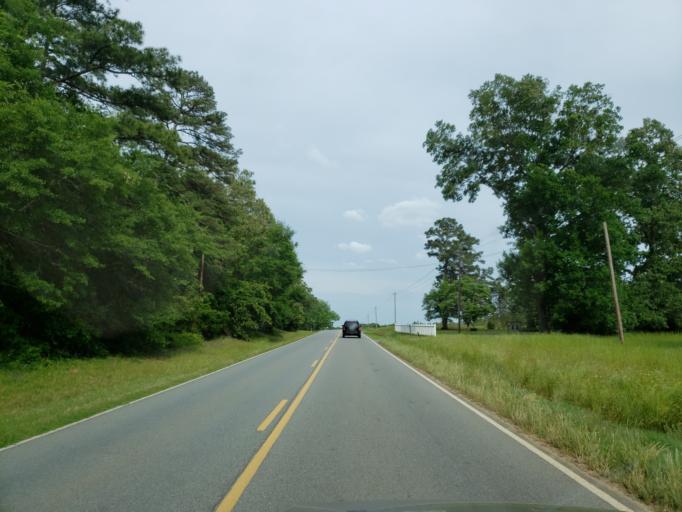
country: US
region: Georgia
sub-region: Dooly County
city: Vienna
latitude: 32.1123
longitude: -83.8506
